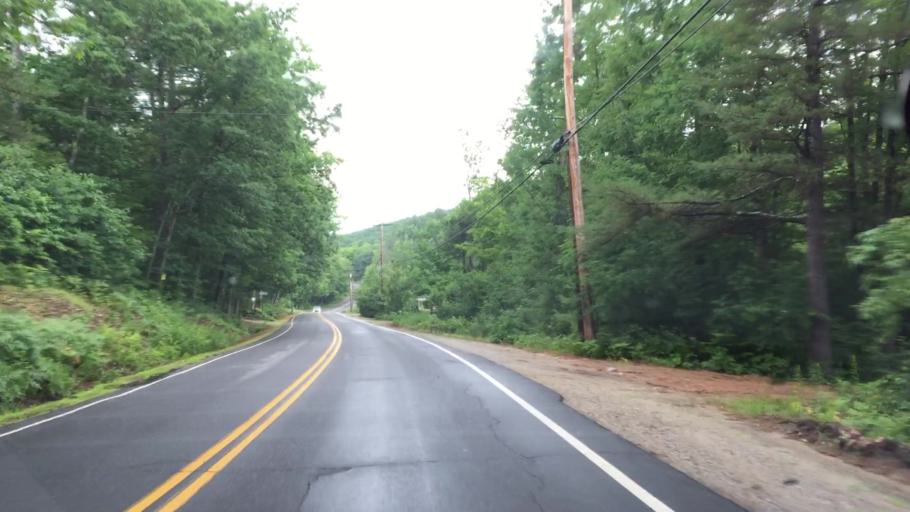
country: US
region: New Hampshire
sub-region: Carroll County
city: Center Harbor
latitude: 43.7420
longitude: -71.4779
